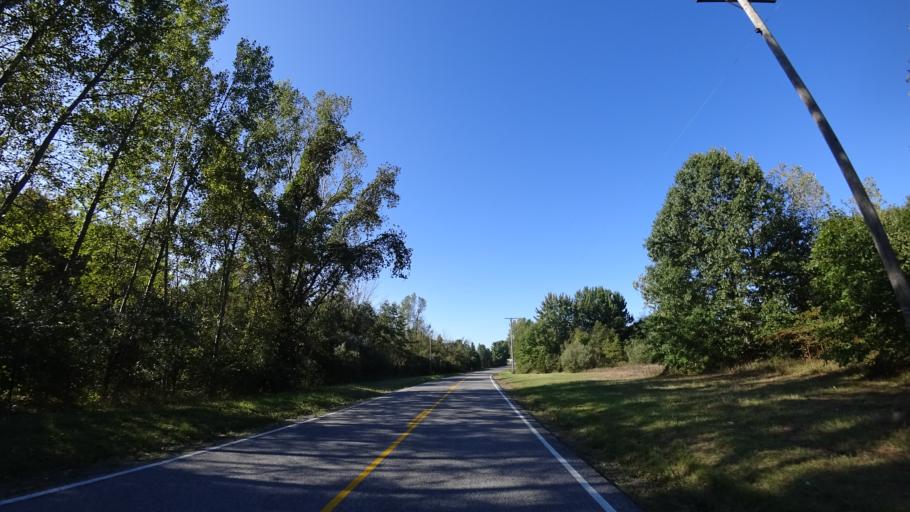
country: US
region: Michigan
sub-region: Berrien County
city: Benton Heights
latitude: 42.1495
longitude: -86.4268
